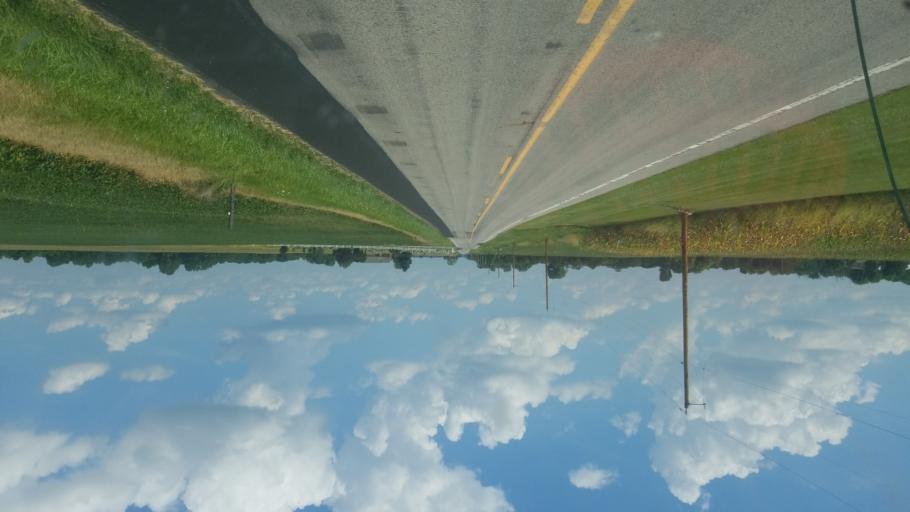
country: US
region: Ohio
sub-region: Hardin County
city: Ada
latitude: 40.7325
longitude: -83.7069
